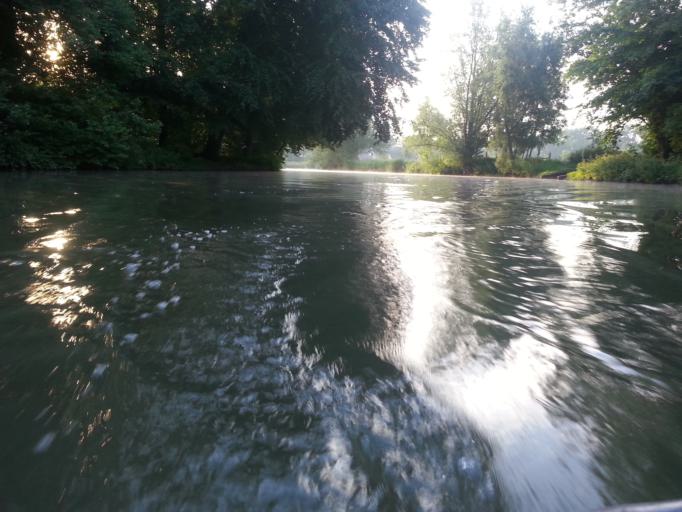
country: NL
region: Utrecht
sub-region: Gemeente Bunnik
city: Bunnik
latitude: 52.0677
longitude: 5.1735
